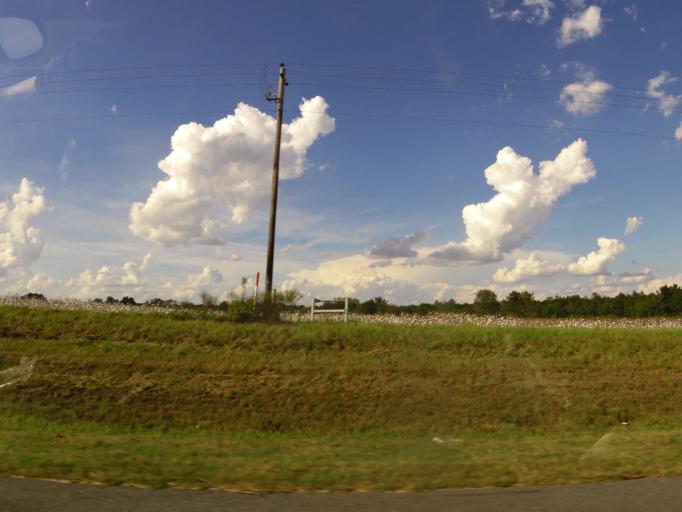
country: US
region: Georgia
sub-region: Brooks County
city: Quitman
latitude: 30.7857
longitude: -83.6035
